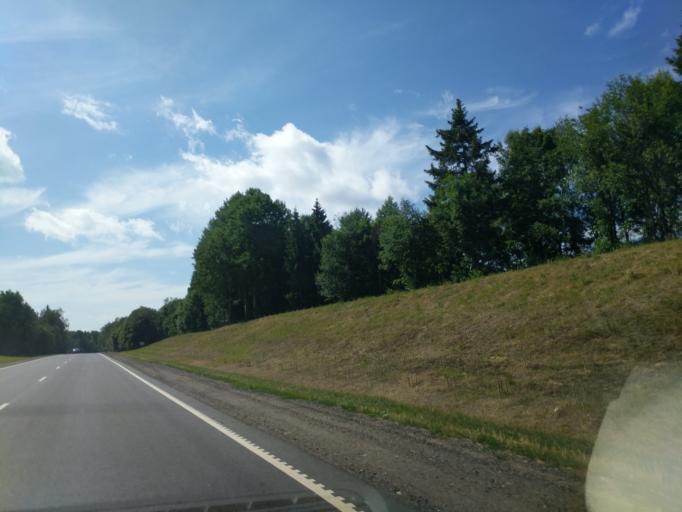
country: BY
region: Minsk
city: Syomkava
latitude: 54.1157
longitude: 27.4055
